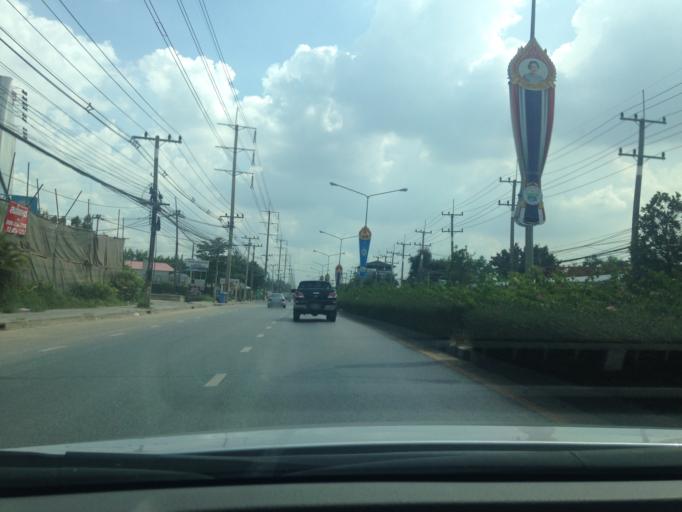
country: TH
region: Pathum Thani
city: Sam Khok
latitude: 14.0628
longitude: 100.5237
